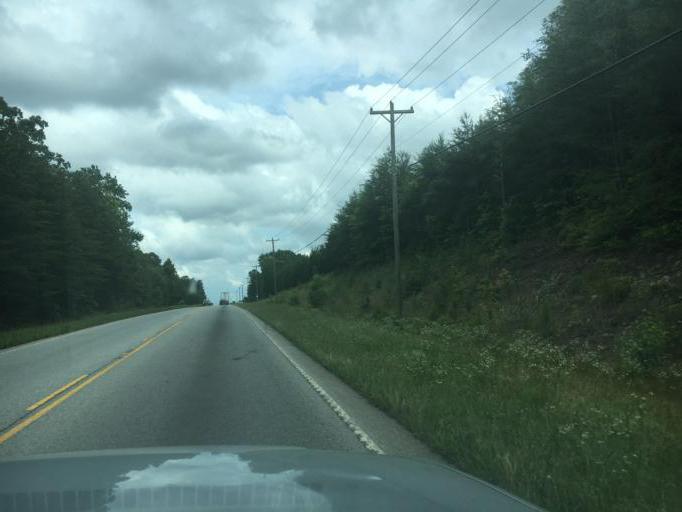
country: US
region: South Carolina
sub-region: Anderson County
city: Williamston
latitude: 34.6356
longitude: -82.4174
